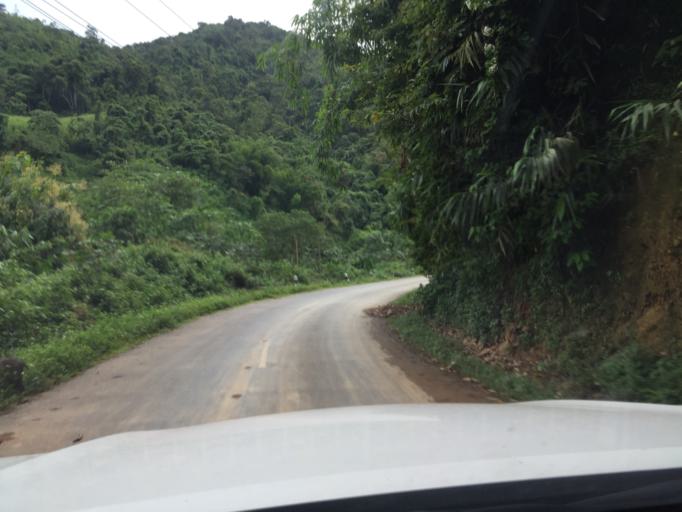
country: LA
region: Oudomxai
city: Muang La
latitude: 21.1102
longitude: 102.2073
